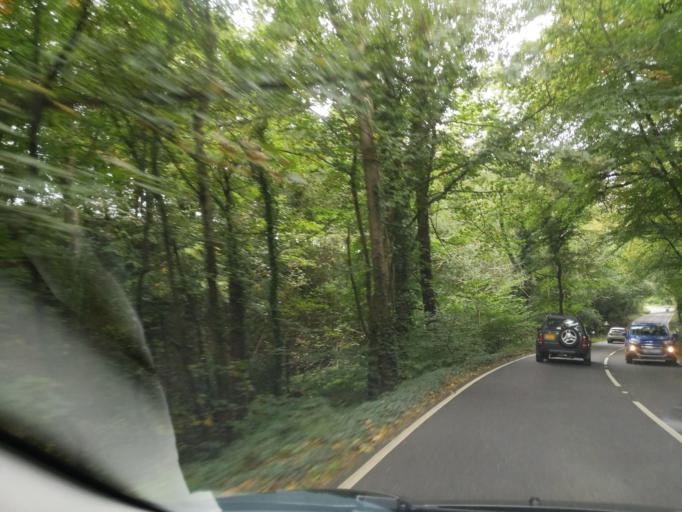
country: GB
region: England
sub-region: Cornwall
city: Helland
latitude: 50.5009
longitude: -4.7759
